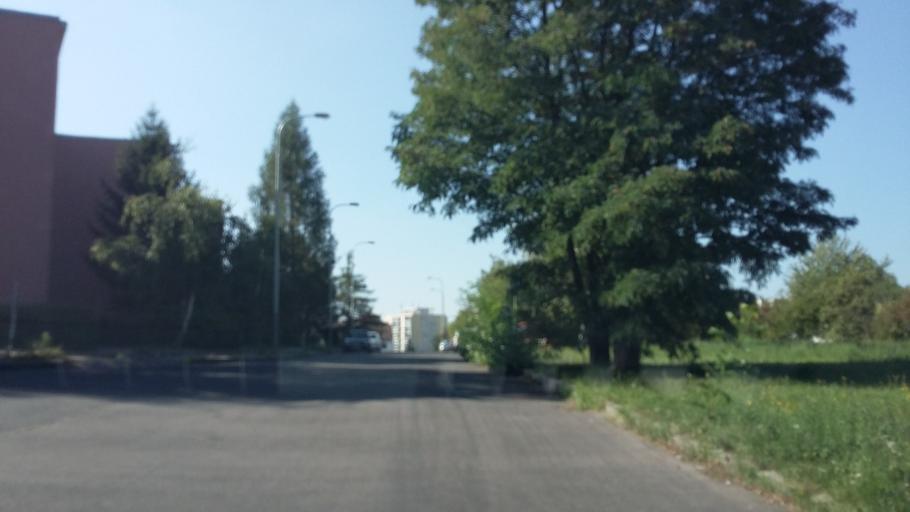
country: CZ
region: Praha
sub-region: Praha 9
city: Vysocany
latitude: 50.0582
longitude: 14.5179
